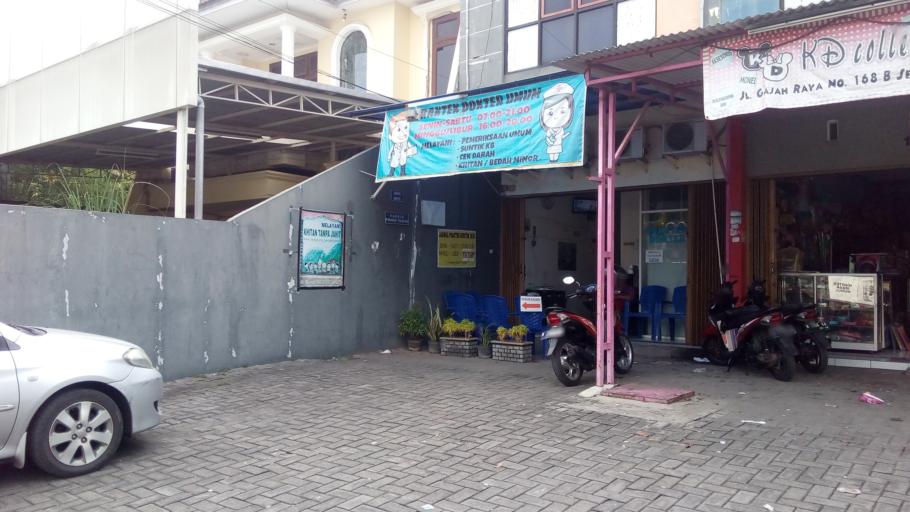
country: ID
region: Central Java
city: Semarang
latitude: -6.9842
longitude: 110.4484
